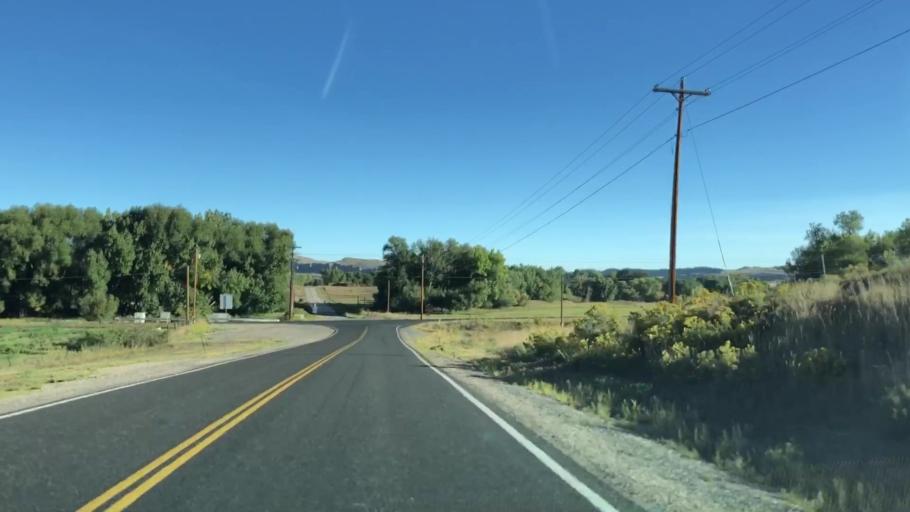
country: US
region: Colorado
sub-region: Larimer County
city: Loveland
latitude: 40.3919
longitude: -105.1631
